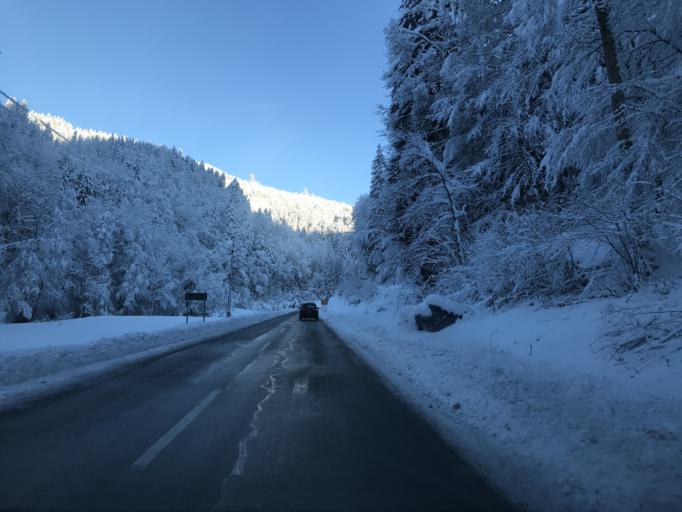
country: DE
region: Baden-Wuerttemberg
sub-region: Freiburg Region
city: Zell im Wiesental
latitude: 47.7464
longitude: 7.8236
